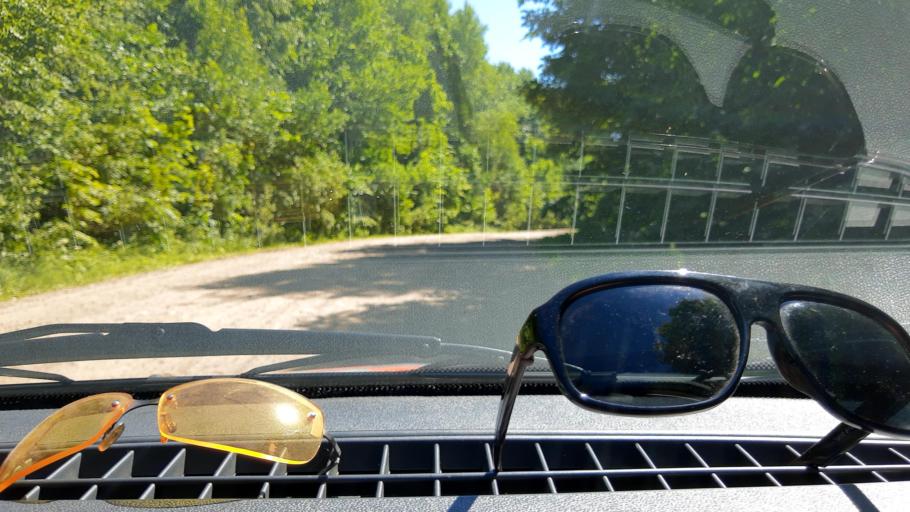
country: RU
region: Bashkortostan
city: Ulu-Telyak
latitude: 54.8060
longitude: 57.0359
